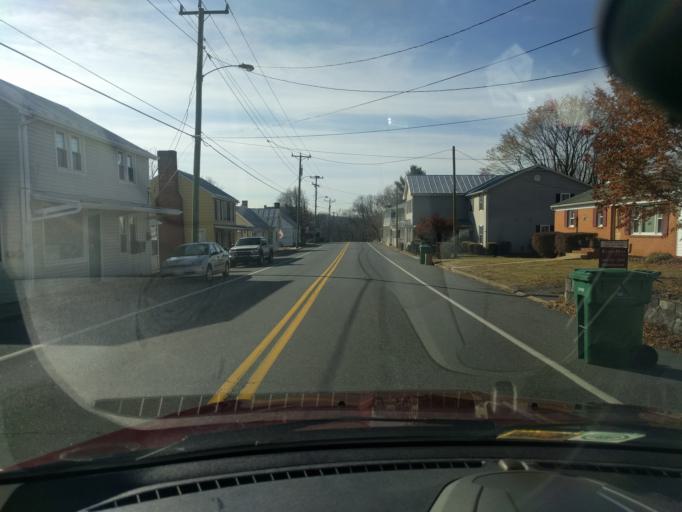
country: US
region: Virginia
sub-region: Rockingham County
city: Bridgewater
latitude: 38.3556
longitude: -78.9430
